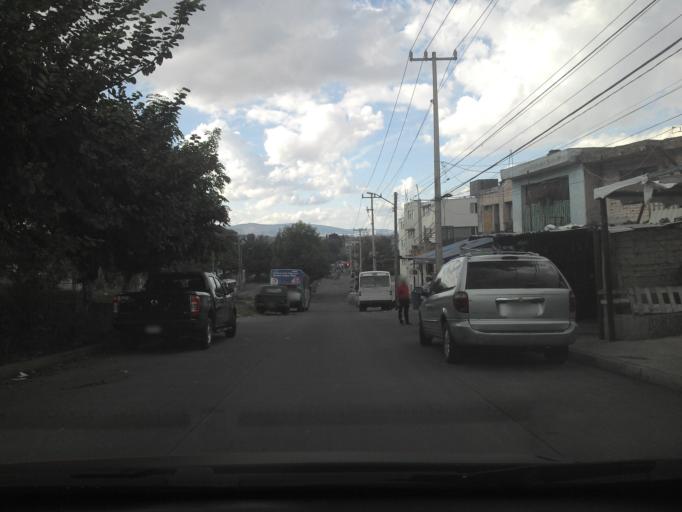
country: MX
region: Jalisco
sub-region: Tlajomulco de Zuniga
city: Altus Bosques
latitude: 20.6168
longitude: -103.3717
